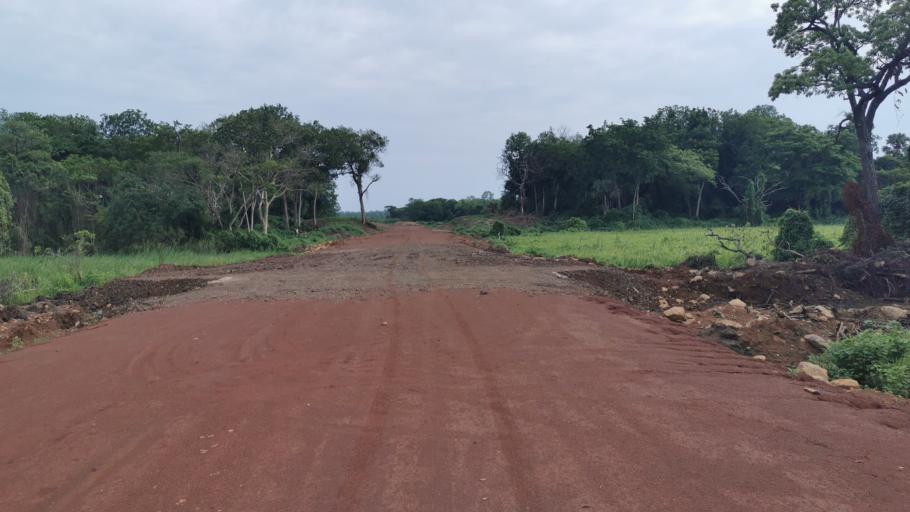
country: ET
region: Gambela
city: Gambela
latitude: 7.8700
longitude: 34.4948
